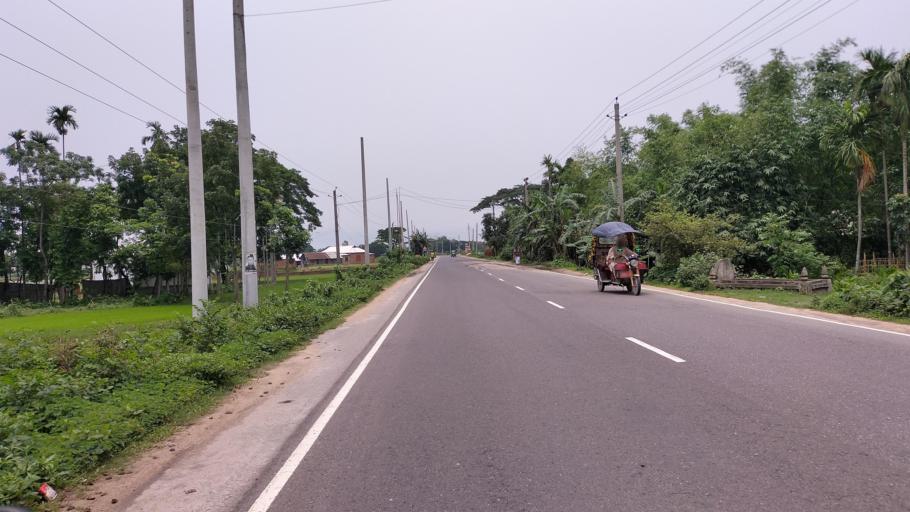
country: BD
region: Dhaka
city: Mymensingh
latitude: 24.7799
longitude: 90.4748
